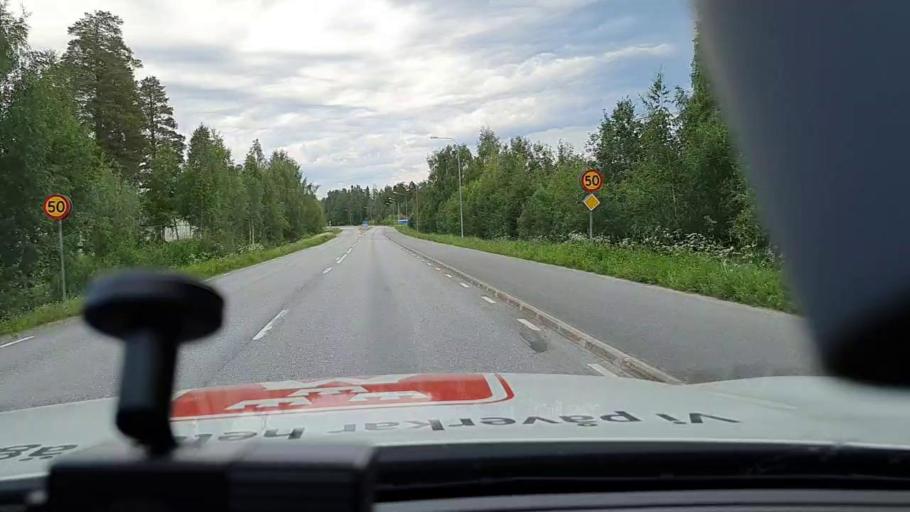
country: SE
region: Norrbotten
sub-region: Bodens Kommun
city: Boden
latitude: 65.8122
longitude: 21.6506
